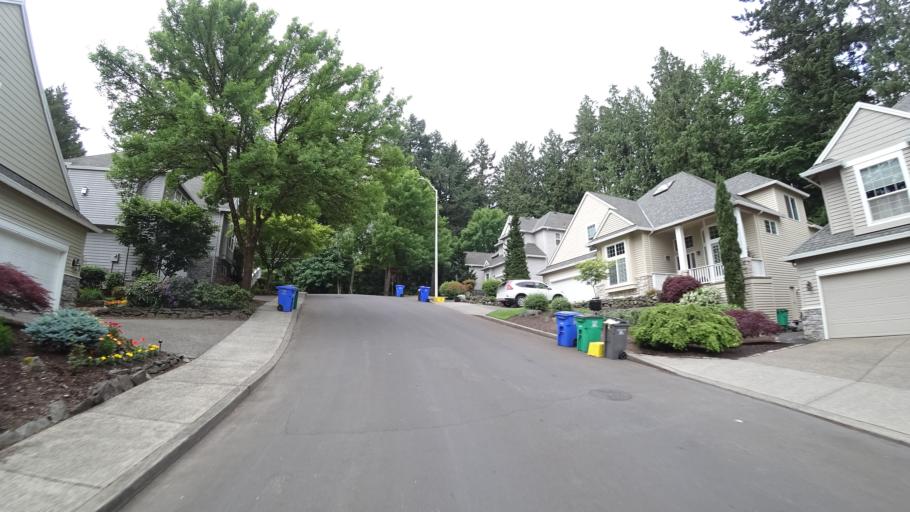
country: US
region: Oregon
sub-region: Washington County
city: Garden Home-Whitford
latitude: 45.4699
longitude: -122.7432
